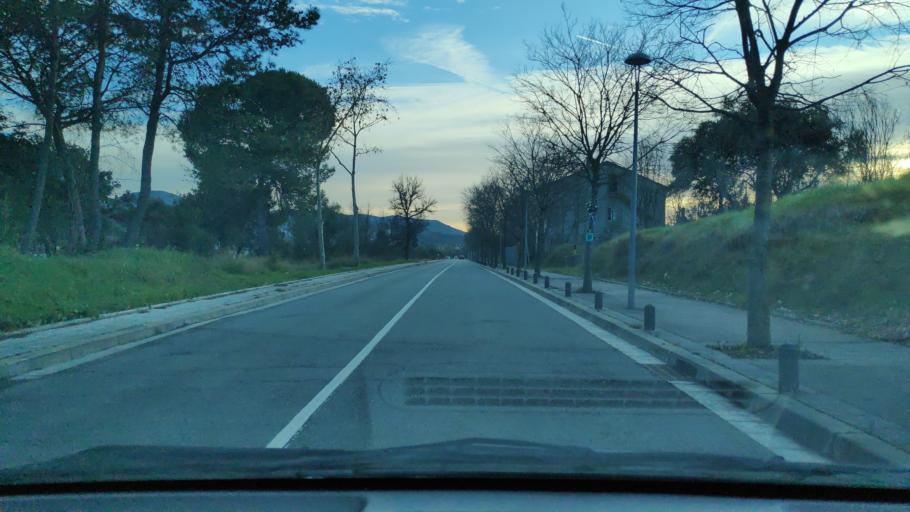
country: ES
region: Catalonia
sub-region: Provincia de Barcelona
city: Montmelo
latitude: 41.5639
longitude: 2.2584
